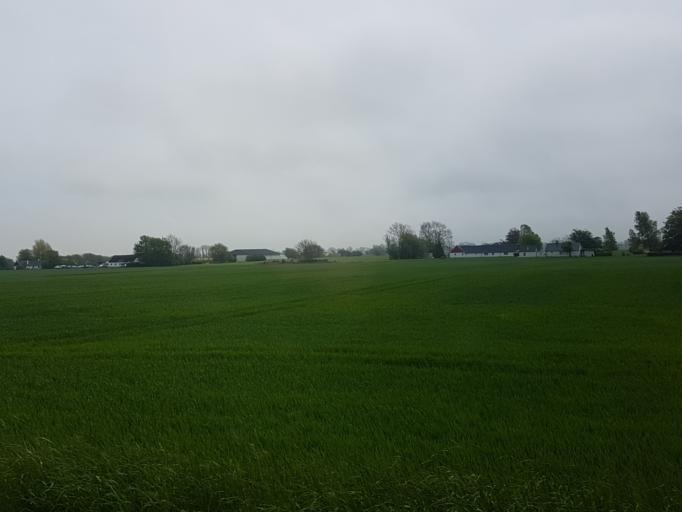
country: SE
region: Skane
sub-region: Ystads Kommun
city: Kopingebro
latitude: 55.4456
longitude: 14.1295
